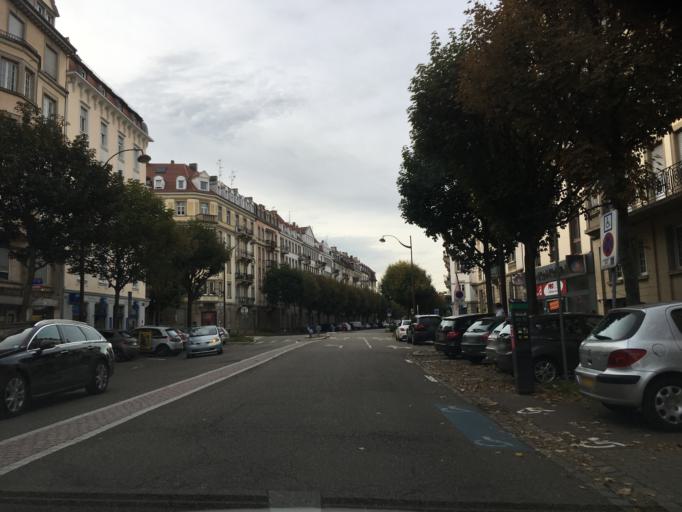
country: FR
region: Alsace
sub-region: Departement du Bas-Rhin
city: Strasbourg
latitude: 48.5858
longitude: 7.7719
